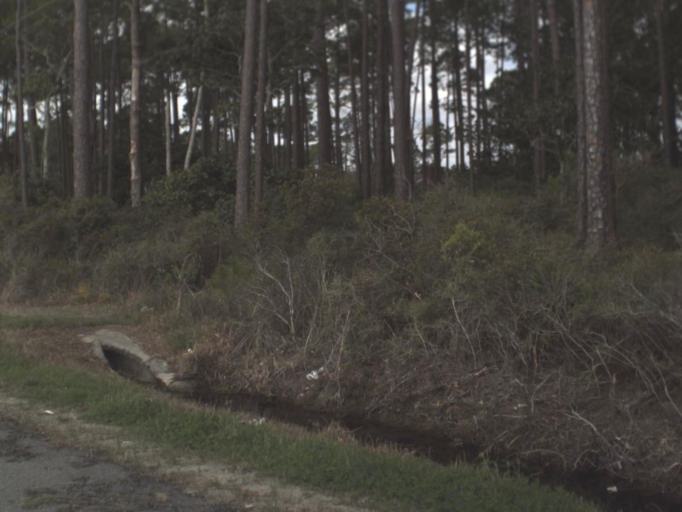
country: US
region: Florida
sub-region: Franklin County
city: Eastpoint
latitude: 29.7491
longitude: -84.8525
